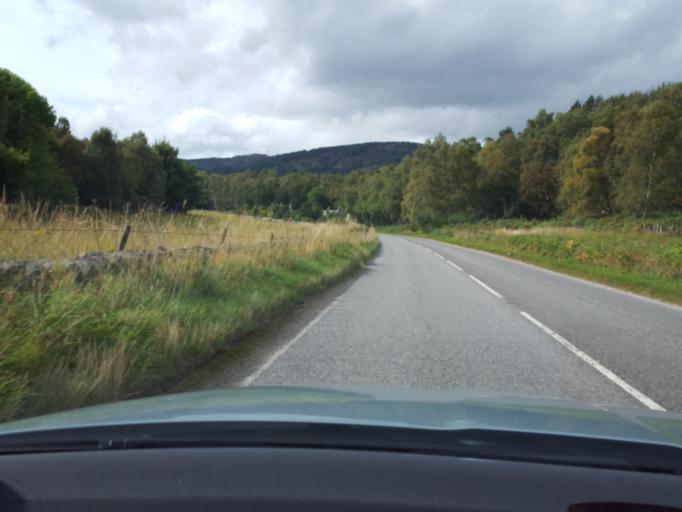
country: GB
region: Scotland
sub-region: Aberdeenshire
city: Ballater
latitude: 57.0705
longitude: -2.9659
